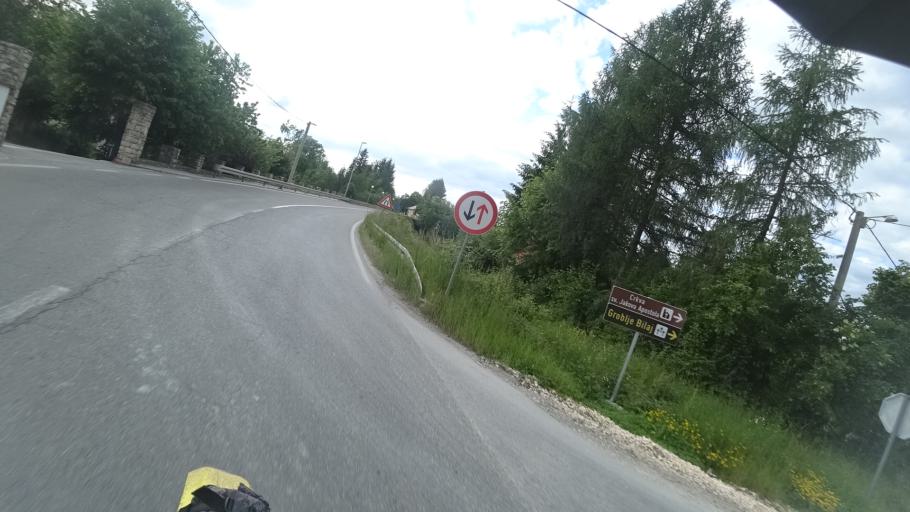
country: HR
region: Licko-Senjska
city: Gospic
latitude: 44.5138
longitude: 15.4239
